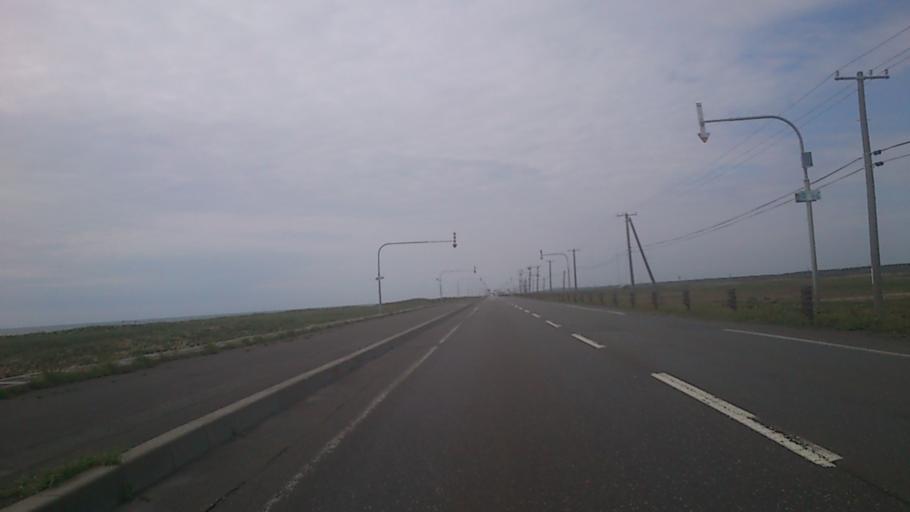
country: JP
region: Hokkaido
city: Makubetsu
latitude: 44.9850
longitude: 141.6910
